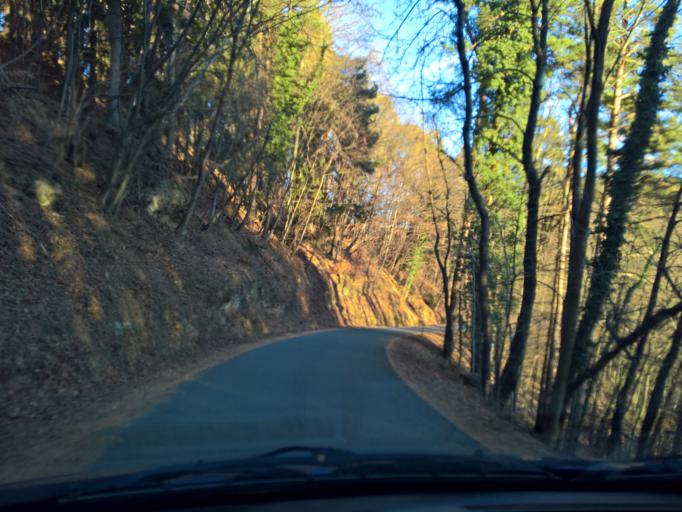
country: AT
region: Styria
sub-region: Politischer Bezirk Leibnitz
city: Leutschach
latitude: 46.6942
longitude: 15.4407
